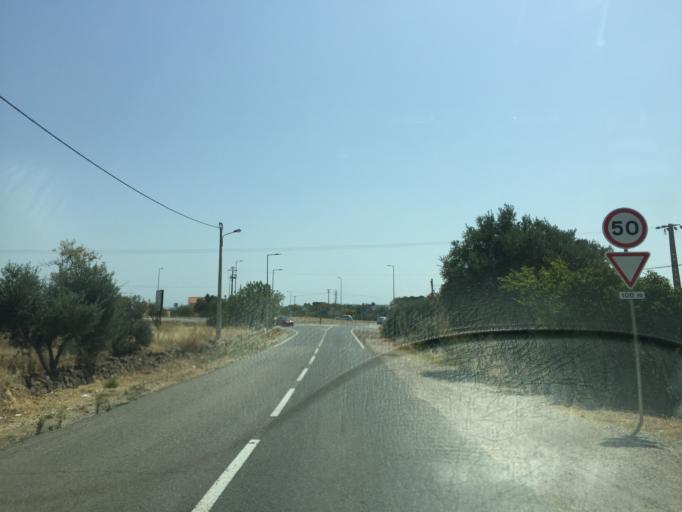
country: PT
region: Faro
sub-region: Loule
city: Boliqueime
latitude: 37.1282
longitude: -8.1595
